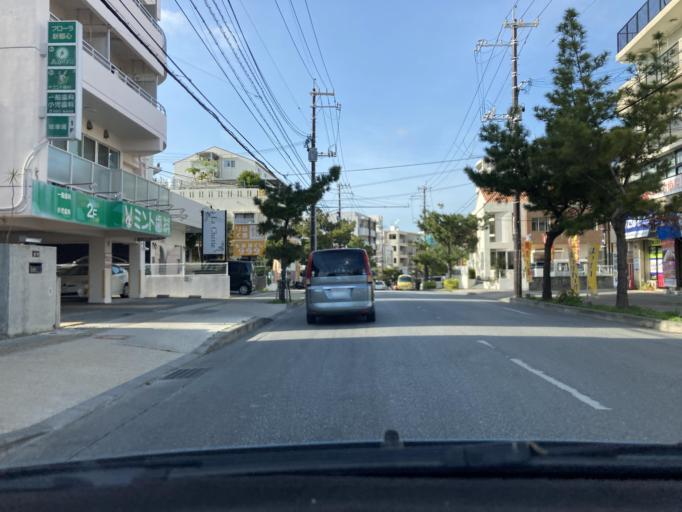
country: JP
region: Okinawa
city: Naha-shi
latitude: 26.2329
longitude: 127.6955
